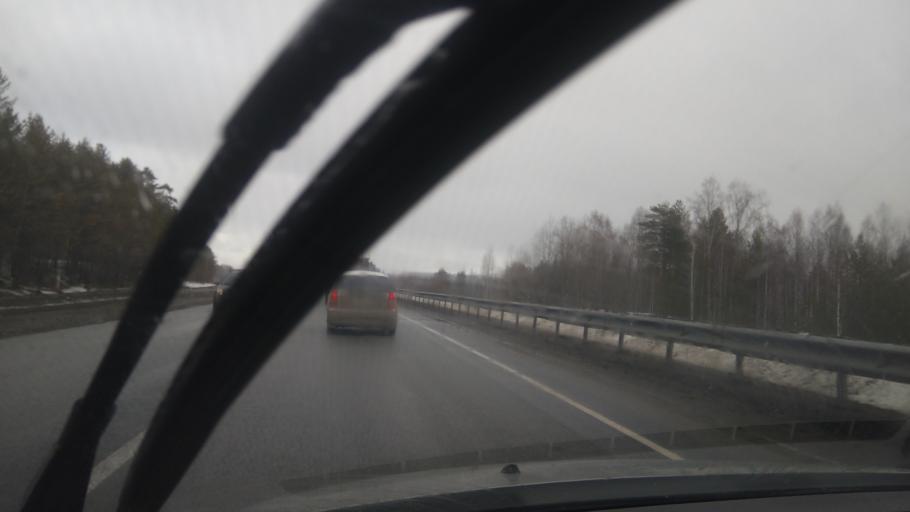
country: RU
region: Sverdlovsk
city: Ufimskiy
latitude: 56.7775
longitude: 58.2553
